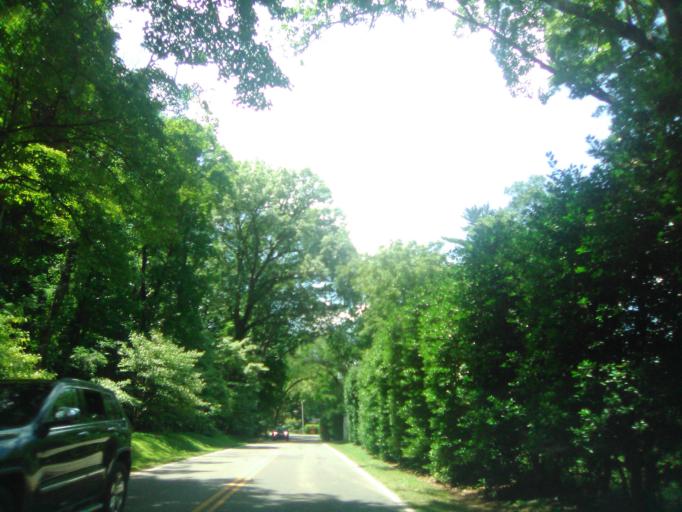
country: US
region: Tennessee
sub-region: Davidson County
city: Belle Meade
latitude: 36.1065
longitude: -86.8515
